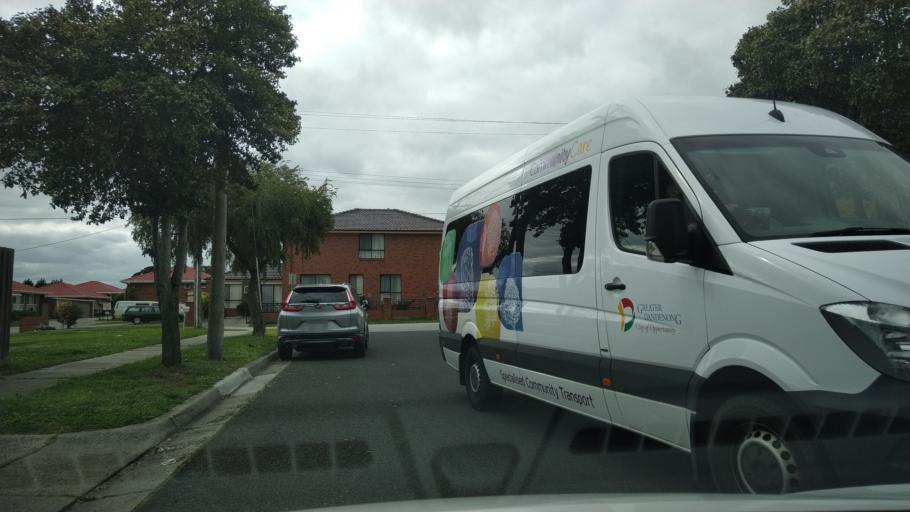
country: AU
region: Victoria
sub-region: Greater Dandenong
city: Springvale South
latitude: -37.9726
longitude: 145.1579
